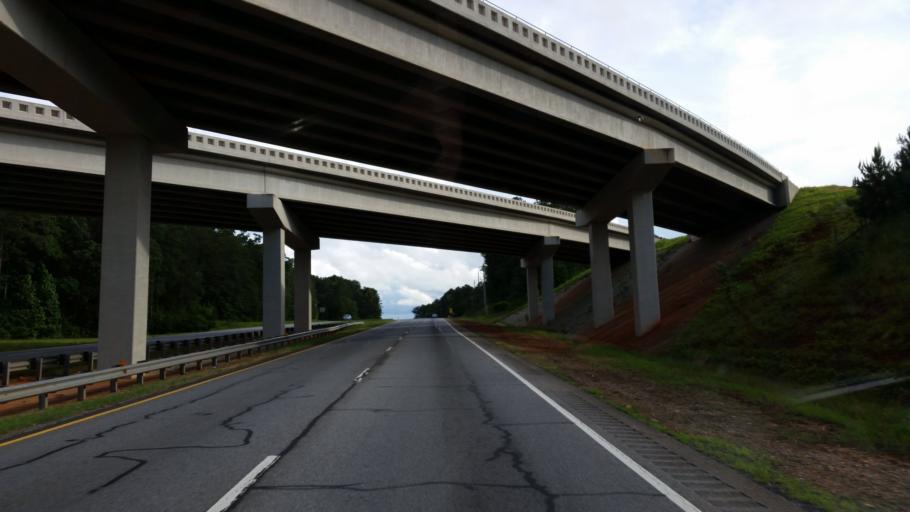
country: US
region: Georgia
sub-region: Bartow County
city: Emerson
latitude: 34.1392
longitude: -84.7498
